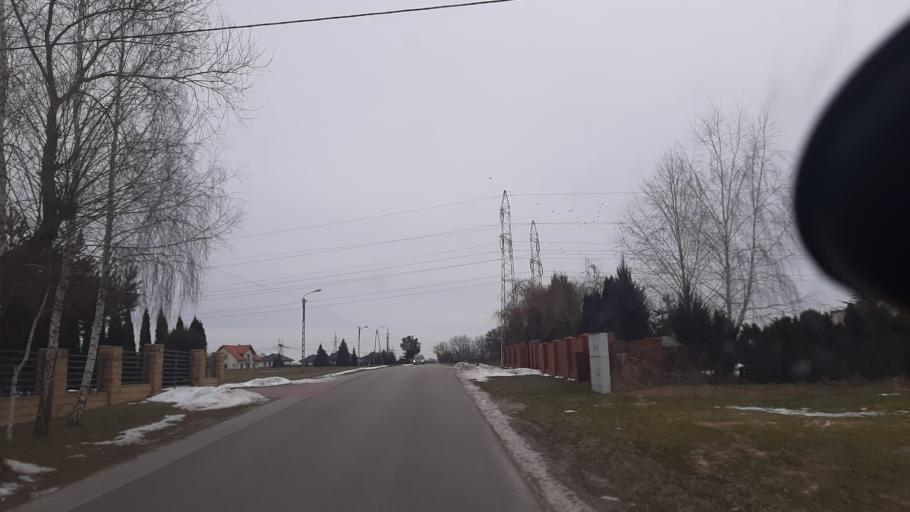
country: PL
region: Lublin Voivodeship
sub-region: Powiat lubelski
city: Jakubowice Murowane
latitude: 51.2907
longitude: 22.6223
